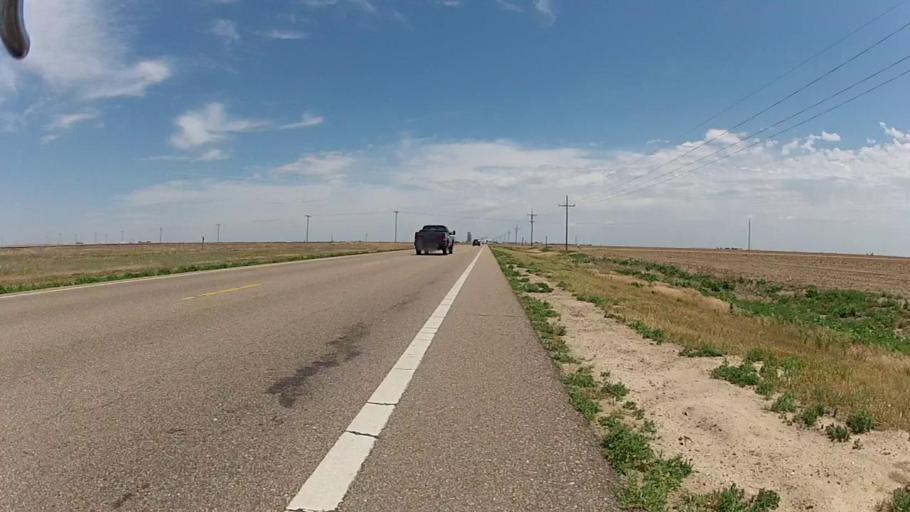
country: US
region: Kansas
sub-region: Haskell County
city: Sublette
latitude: 37.4703
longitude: -100.8906
